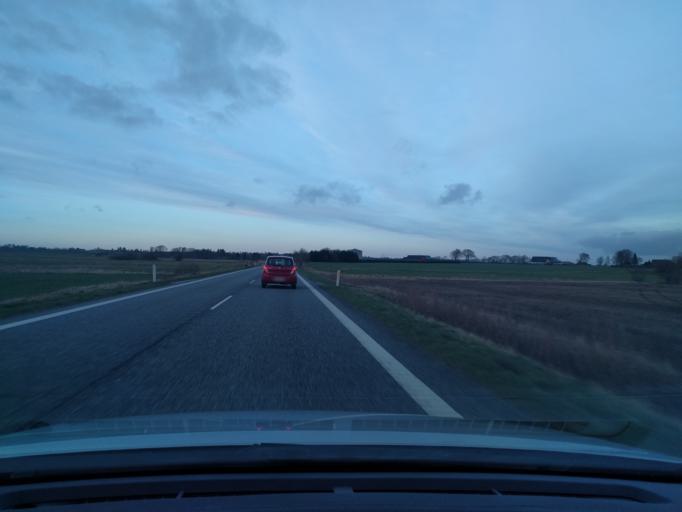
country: DK
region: South Denmark
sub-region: Tonder Kommune
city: Toftlund
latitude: 55.1639
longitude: 9.0459
